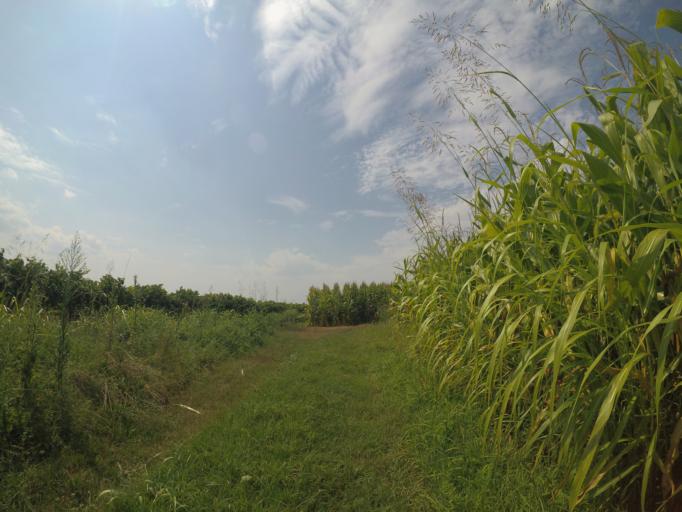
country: IT
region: Friuli Venezia Giulia
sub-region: Provincia di Udine
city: Bertiolo
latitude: 45.9555
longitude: 13.0642
